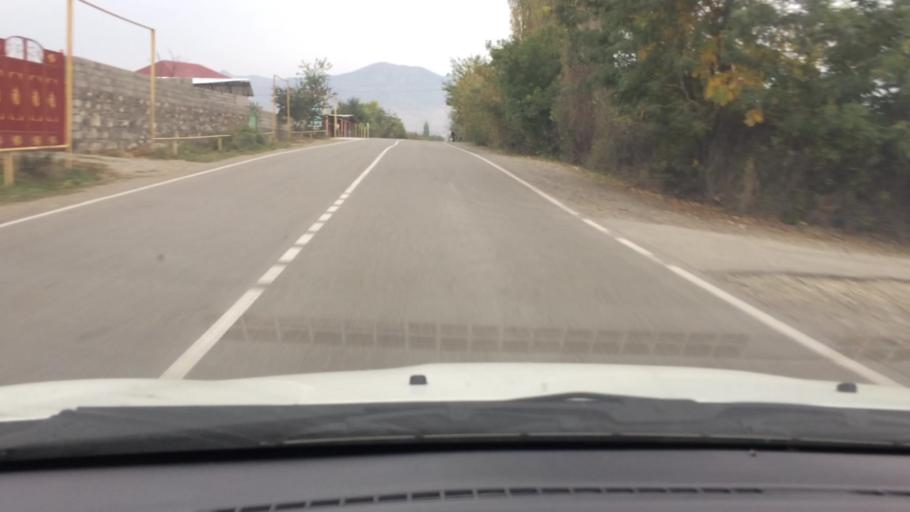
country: AM
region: Tavush
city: Bagratashen
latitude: 41.2360
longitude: 44.8073
